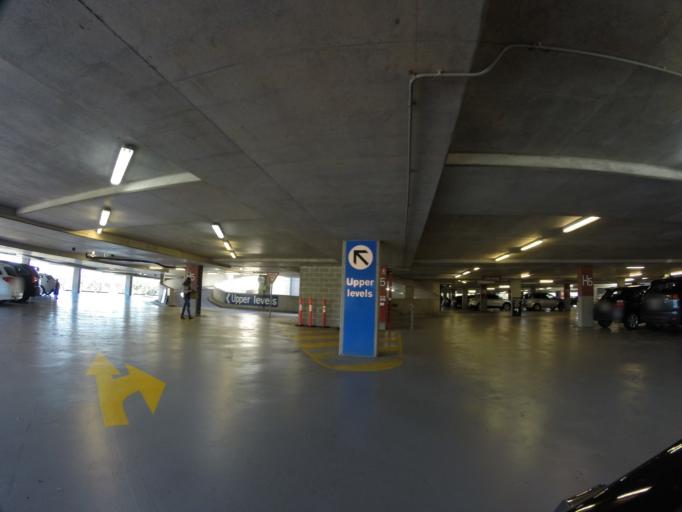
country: AU
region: New South Wales
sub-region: Canada Bay
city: Concord West
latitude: -33.8463
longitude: 151.0617
